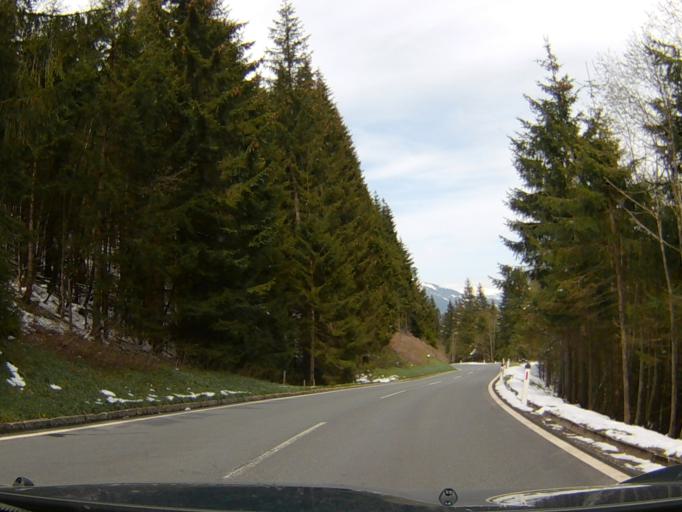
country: AT
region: Salzburg
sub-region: Politischer Bezirk Zell am See
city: Krimml
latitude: 47.2193
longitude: 12.1535
